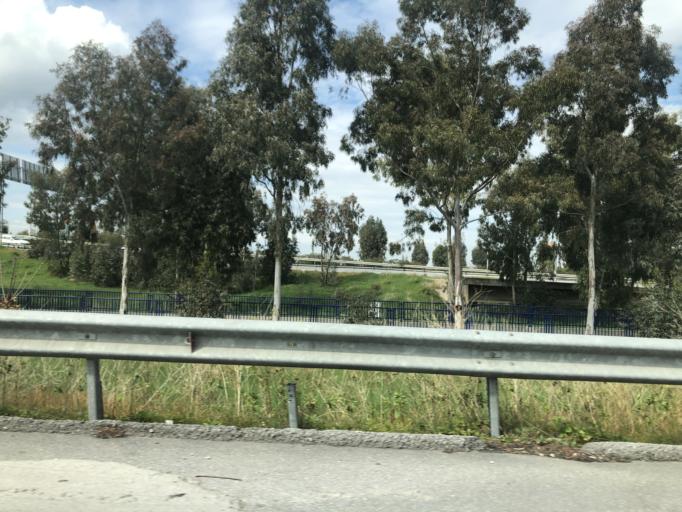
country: TR
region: Izmir
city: Karabaglar
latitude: 38.3983
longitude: 27.0652
